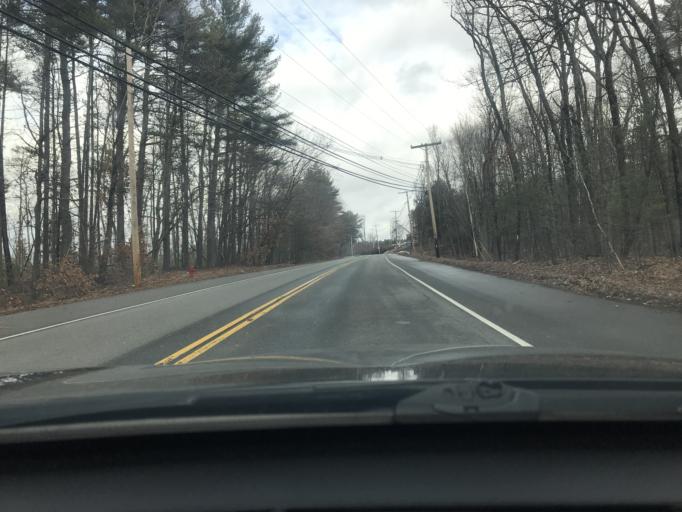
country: US
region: Massachusetts
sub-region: Middlesex County
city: Tyngsboro
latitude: 42.6635
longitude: -71.4240
